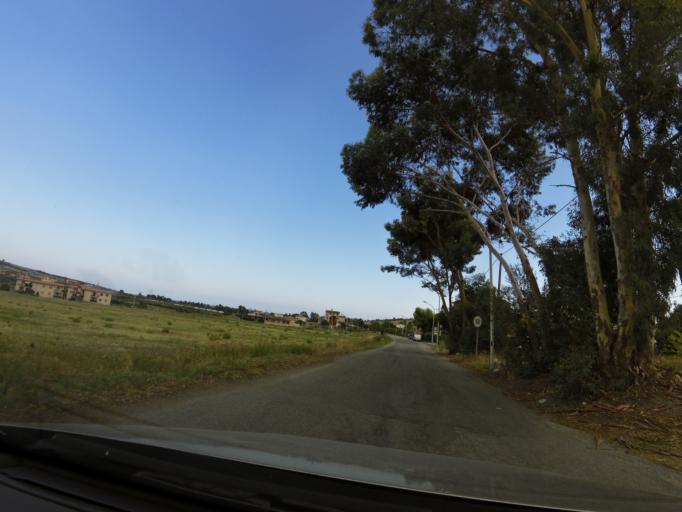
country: IT
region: Calabria
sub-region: Provincia di Reggio Calabria
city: Monasterace
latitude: 38.4236
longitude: 16.5402
